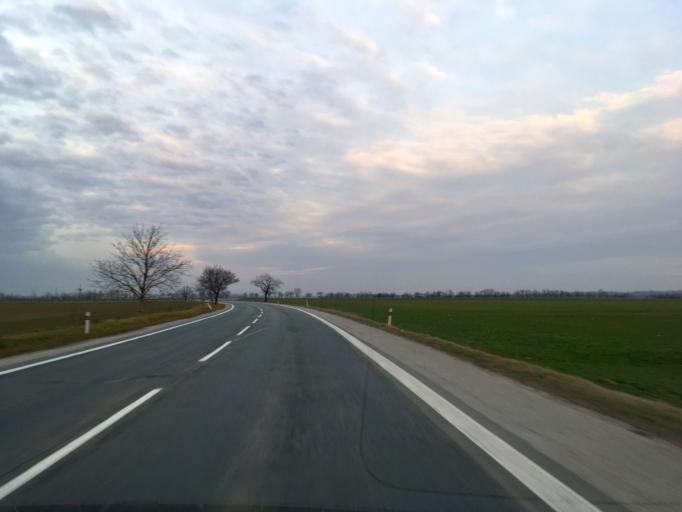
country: HU
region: Komarom-Esztergom
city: Acs
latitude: 47.7647
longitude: 17.9858
